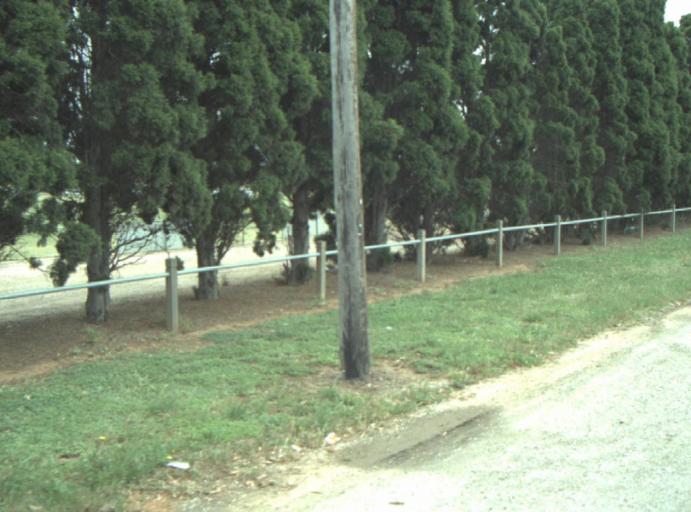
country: AU
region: Victoria
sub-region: Greater Geelong
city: Lara
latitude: -38.0202
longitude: 144.4146
